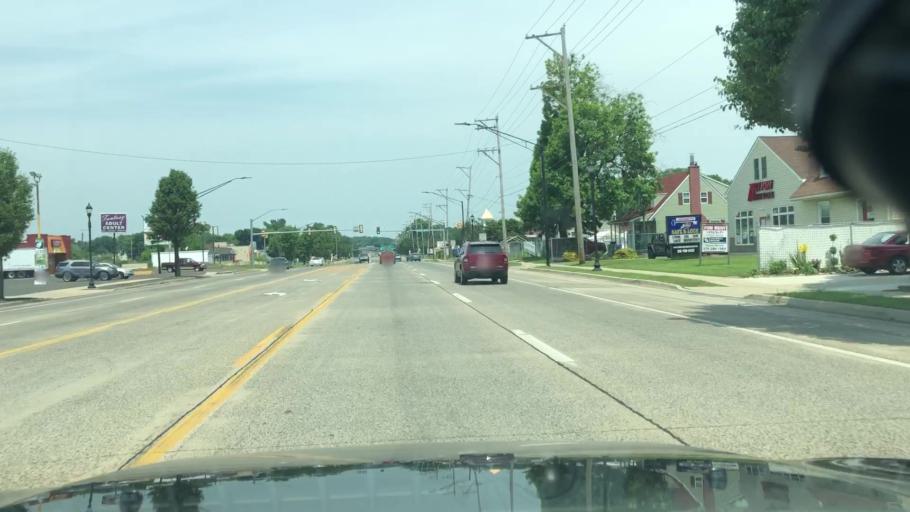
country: US
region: Pennsylvania
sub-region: Bucks County
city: Bristol
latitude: 40.1059
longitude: -74.8764
